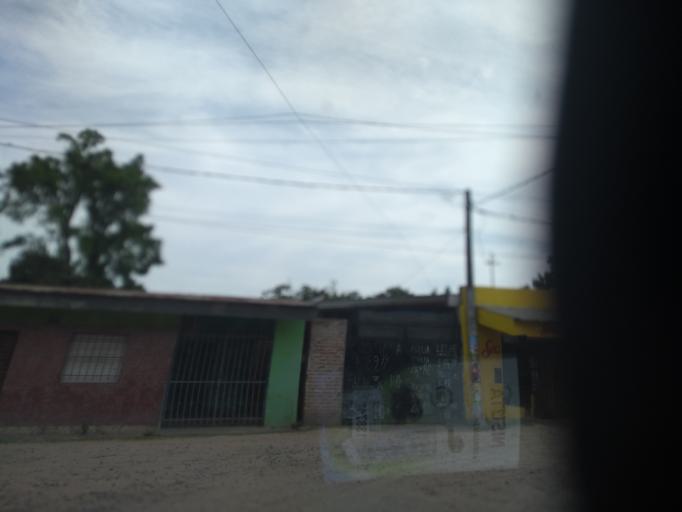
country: AR
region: Chaco
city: Resistencia
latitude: -27.4735
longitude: -58.9722
